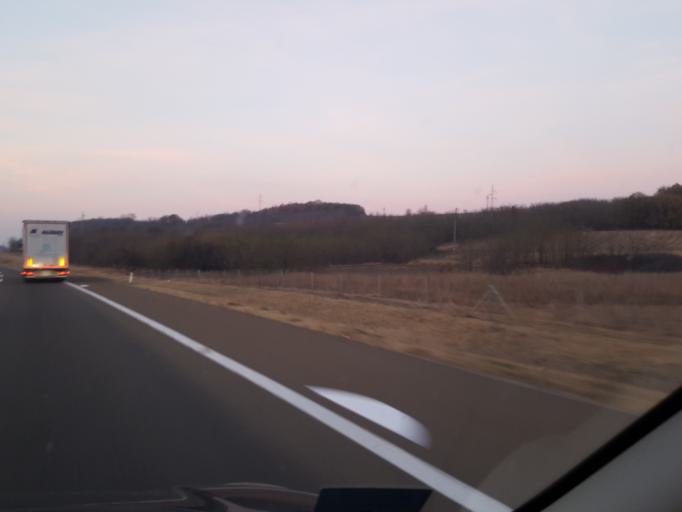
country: RS
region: Central Serbia
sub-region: Rasinski Okrug
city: Cicevac
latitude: 43.7824
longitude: 21.4386
